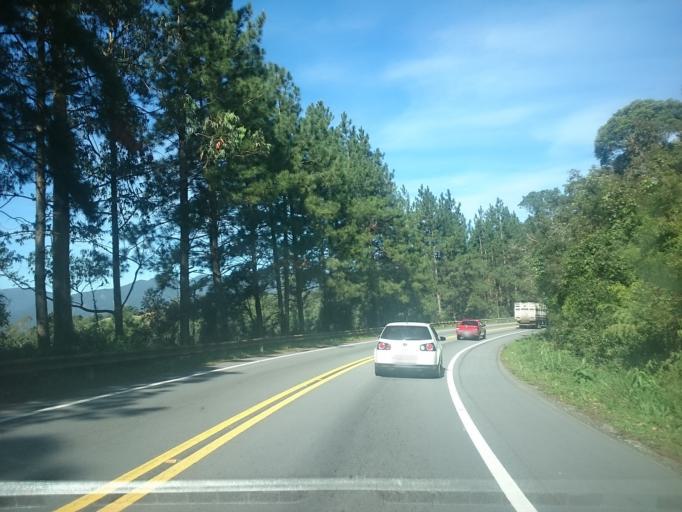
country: BR
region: Santa Catarina
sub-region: Santo Amaro Da Imperatriz
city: Santo Amaro da Imperatriz
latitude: -27.7127
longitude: -48.9439
